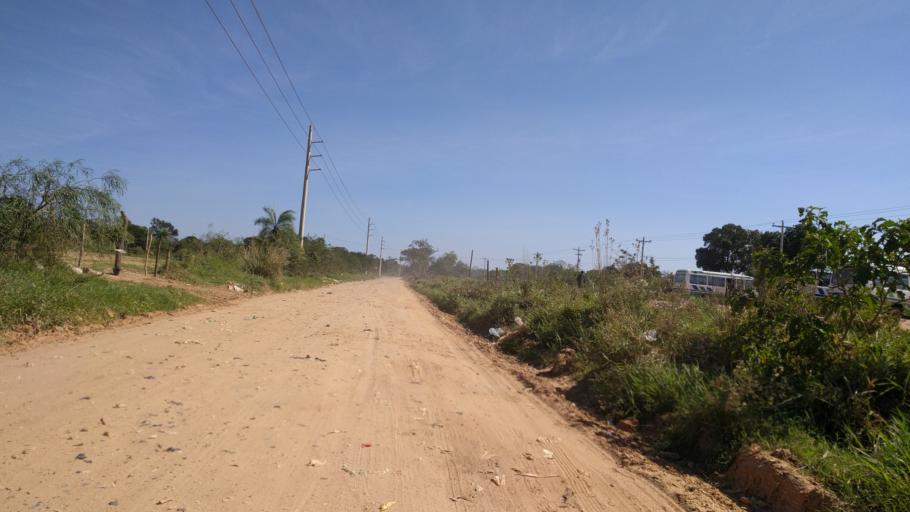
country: BO
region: Santa Cruz
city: Santa Cruz de la Sierra
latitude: -17.8609
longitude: -63.2087
